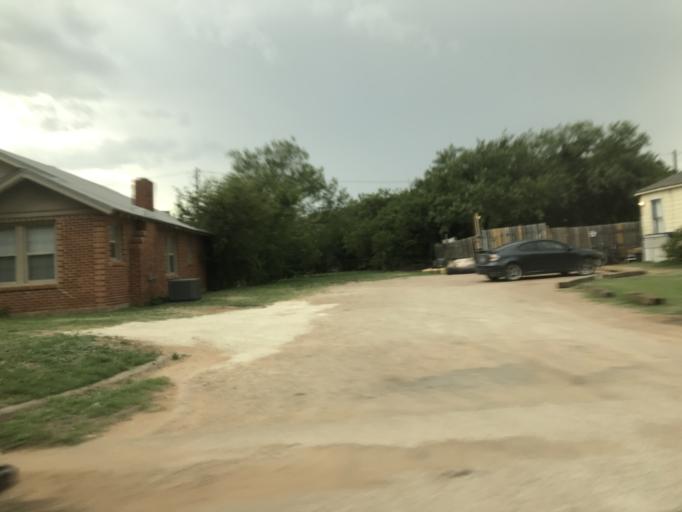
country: US
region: Texas
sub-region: Taylor County
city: Abilene
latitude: 32.4467
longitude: -99.7565
